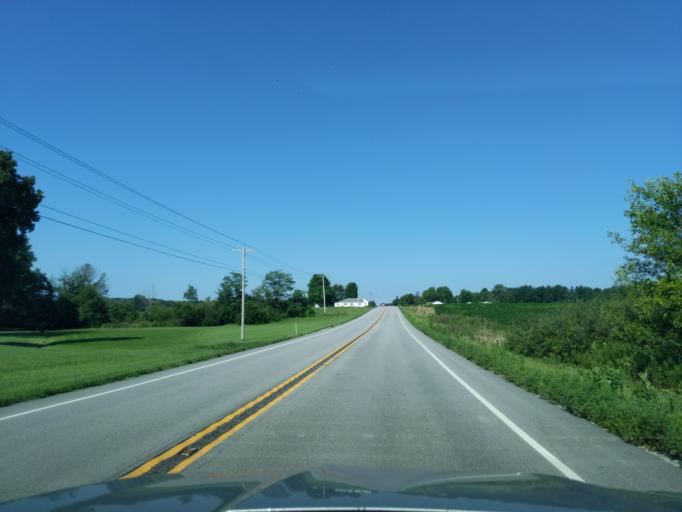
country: US
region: Indiana
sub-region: Ripley County
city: Versailles
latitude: 39.0748
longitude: -85.3073
